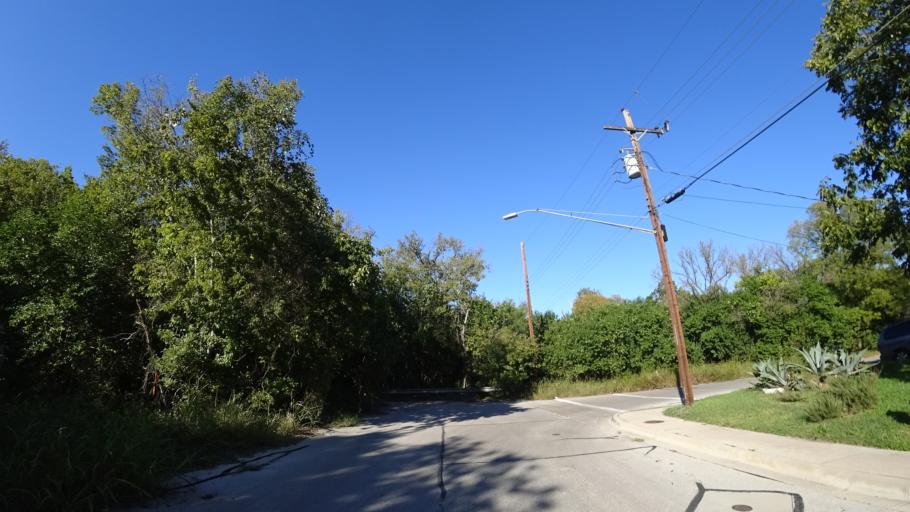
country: US
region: Texas
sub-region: Travis County
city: Austin
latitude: 30.2265
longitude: -97.7338
